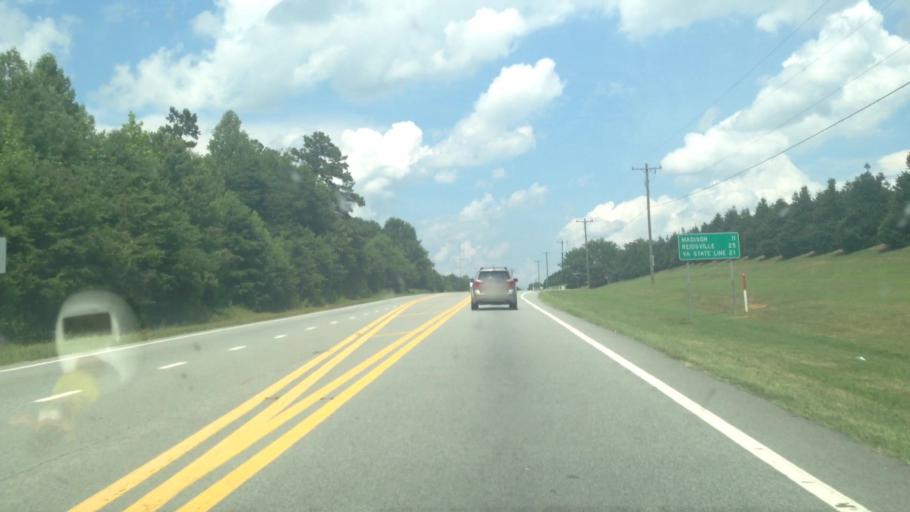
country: US
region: North Carolina
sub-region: Guilford County
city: Stokesdale
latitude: 36.2486
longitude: -79.9695
